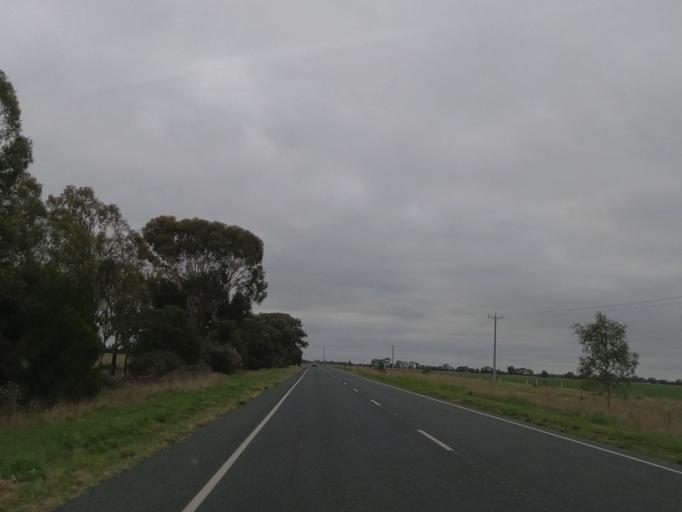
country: AU
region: Victoria
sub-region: Greater Bendigo
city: Long Gully
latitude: -36.3529
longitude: 143.9771
